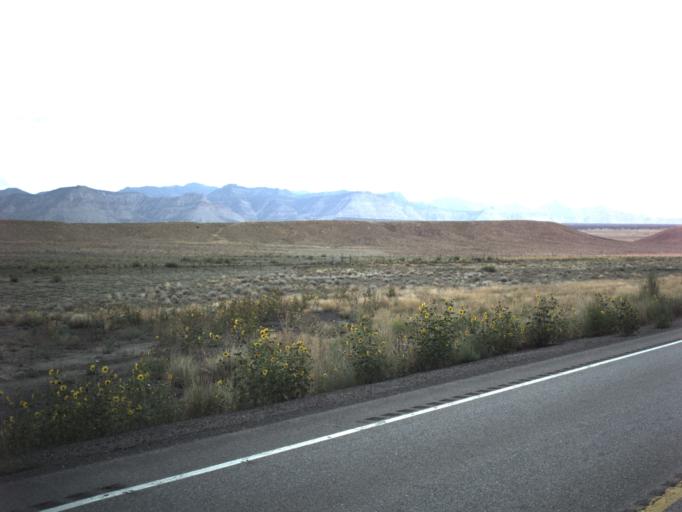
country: US
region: Utah
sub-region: Carbon County
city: East Carbon City
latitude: 39.4624
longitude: -110.4890
